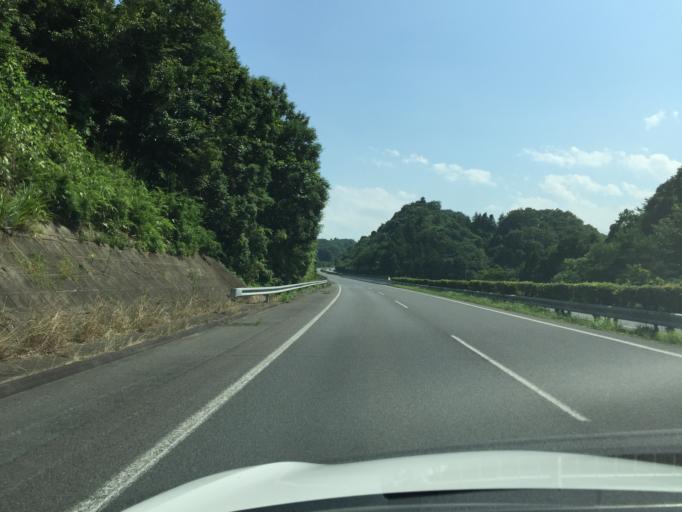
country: JP
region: Fukushima
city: Iwaki
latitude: 36.9800
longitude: 140.7959
